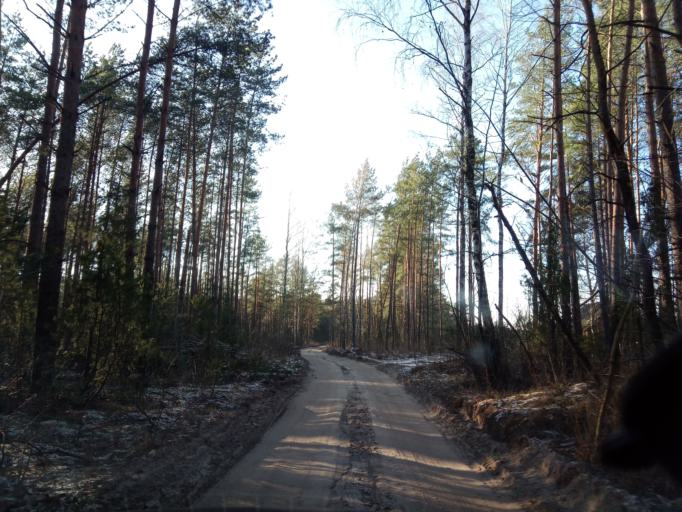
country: LT
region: Alytaus apskritis
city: Druskininkai
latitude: 53.9521
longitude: 23.8823
